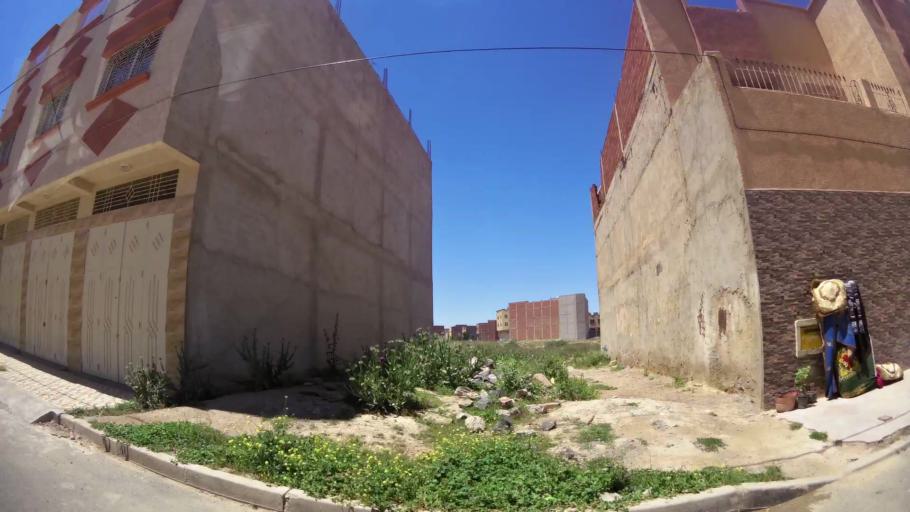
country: MA
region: Oriental
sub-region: Oujda-Angad
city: Oujda
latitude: 34.6790
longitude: -1.8635
